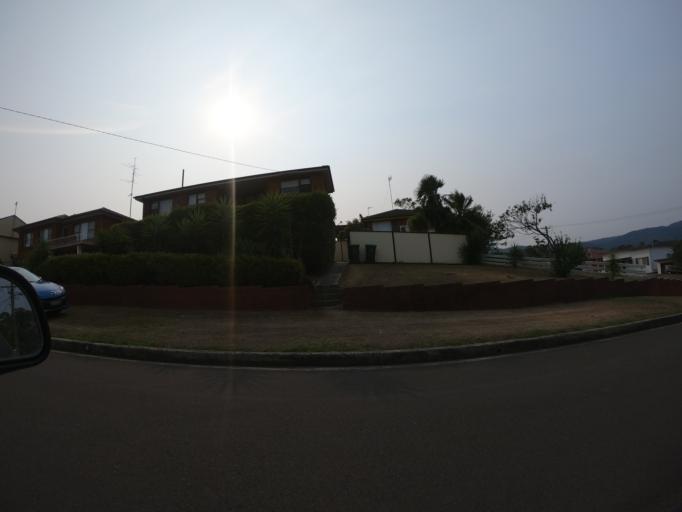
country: AU
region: New South Wales
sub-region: Wollongong
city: Cordeaux Heights
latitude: -34.4536
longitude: 150.8390
